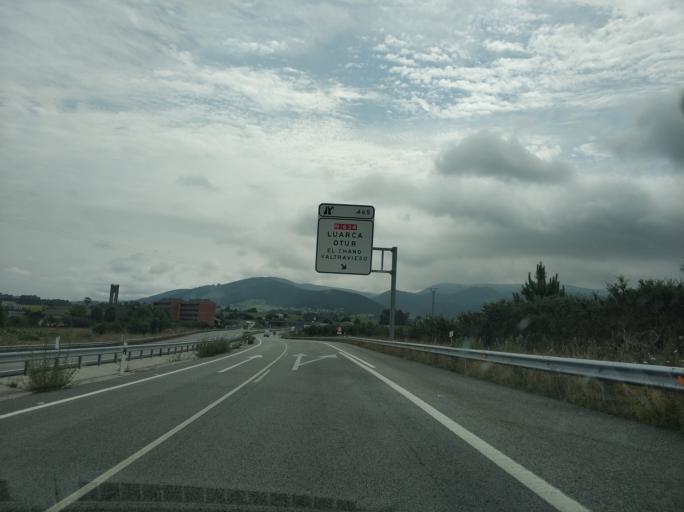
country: ES
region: Asturias
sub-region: Province of Asturias
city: Navia
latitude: 43.5286
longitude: -6.5588
